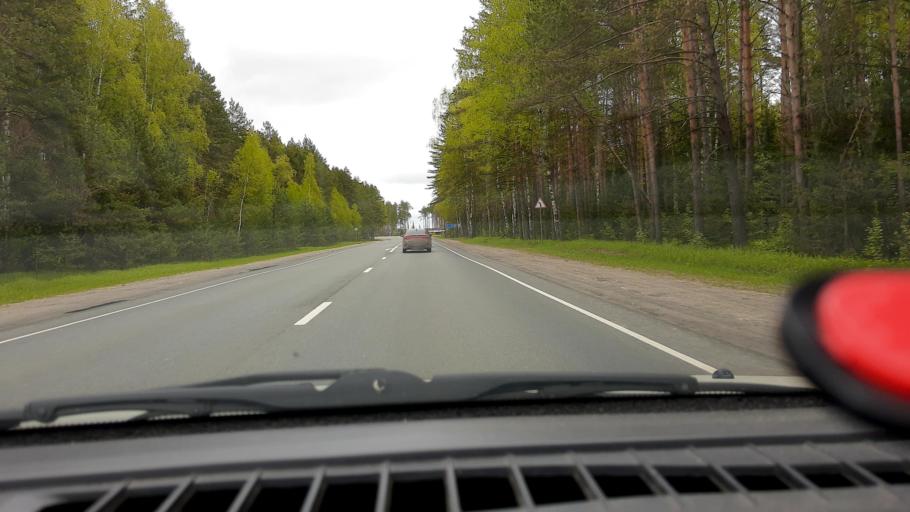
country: RU
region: Nizjnij Novgorod
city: Linda
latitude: 56.6843
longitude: 44.1713
